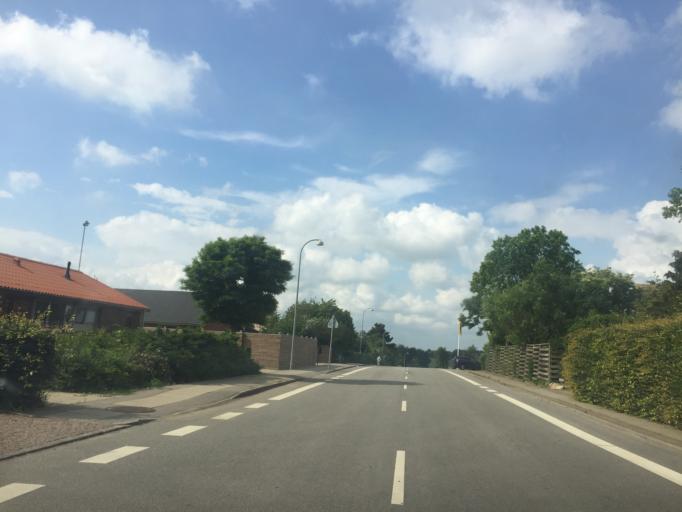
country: DK
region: Capital Region
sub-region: Hoje-Taastrup Kommune
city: Flong
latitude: 55.6941
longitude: 12.1603
